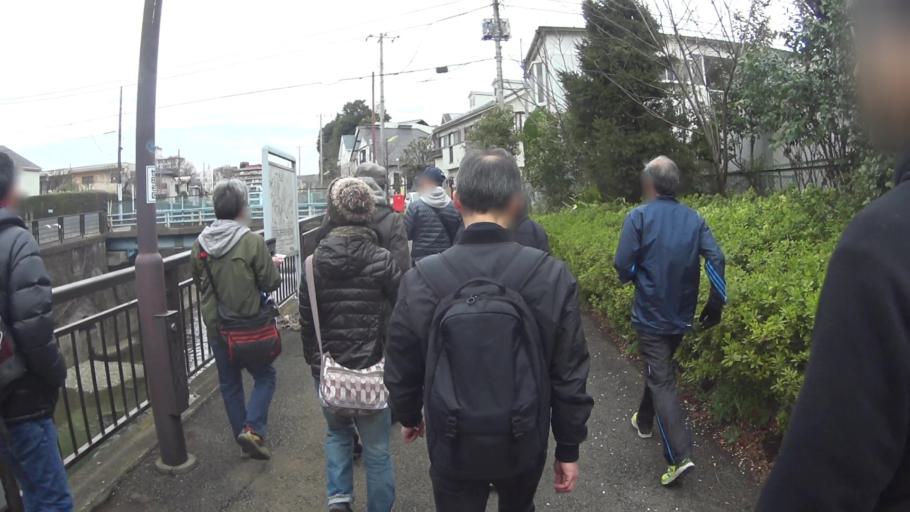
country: JP
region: Tokyo
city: Chofugaoka
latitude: 35.6380
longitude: 139.6043
